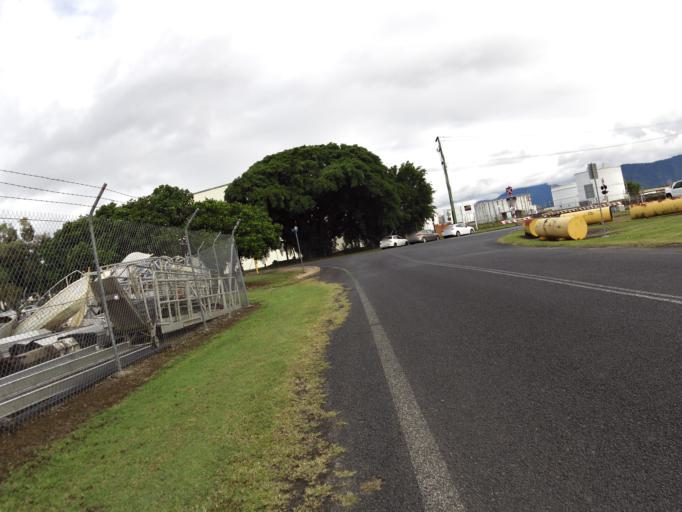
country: AU
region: Queensland
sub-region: Cairns
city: Cairns
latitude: -16.9299
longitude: 145.7779
